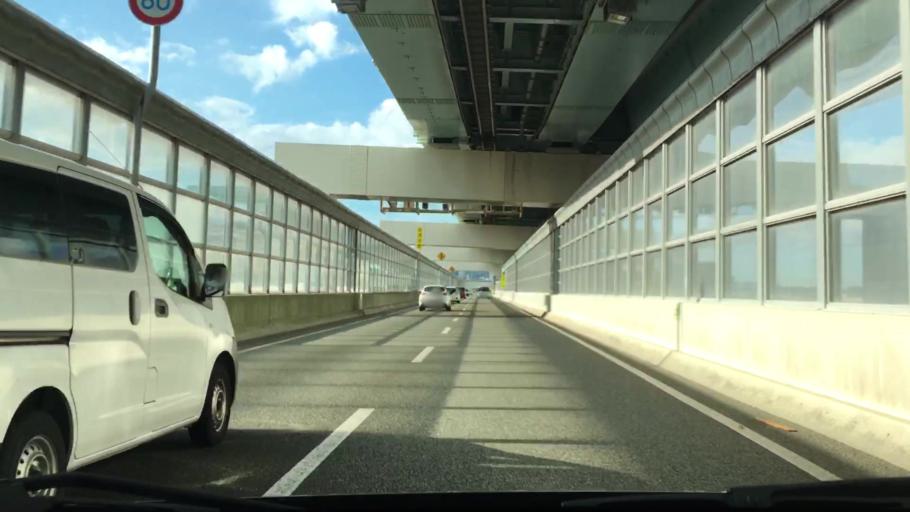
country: JP
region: Fukuoka
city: Fukuoka-shi
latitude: 33.5727
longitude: 130.3165
